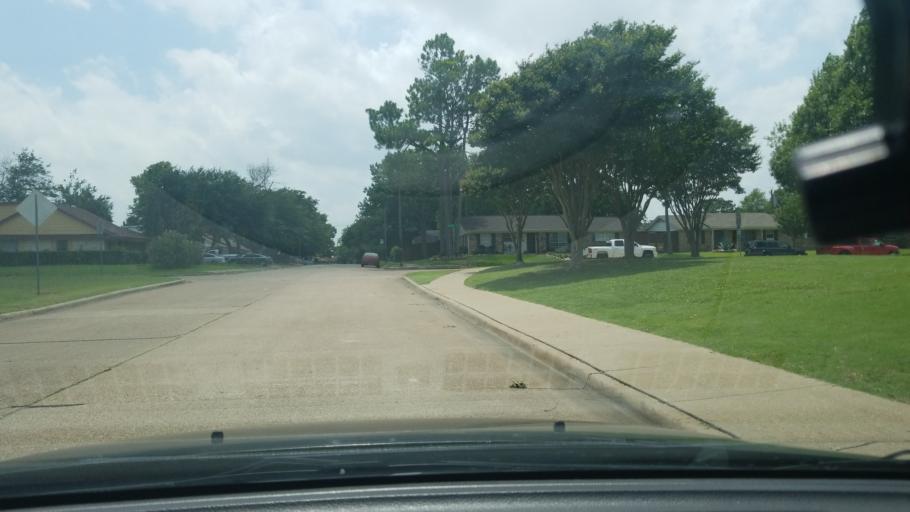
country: US
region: Texas
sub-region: Dallas County
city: Mesquite
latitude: 32.7957
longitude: -96.6447
